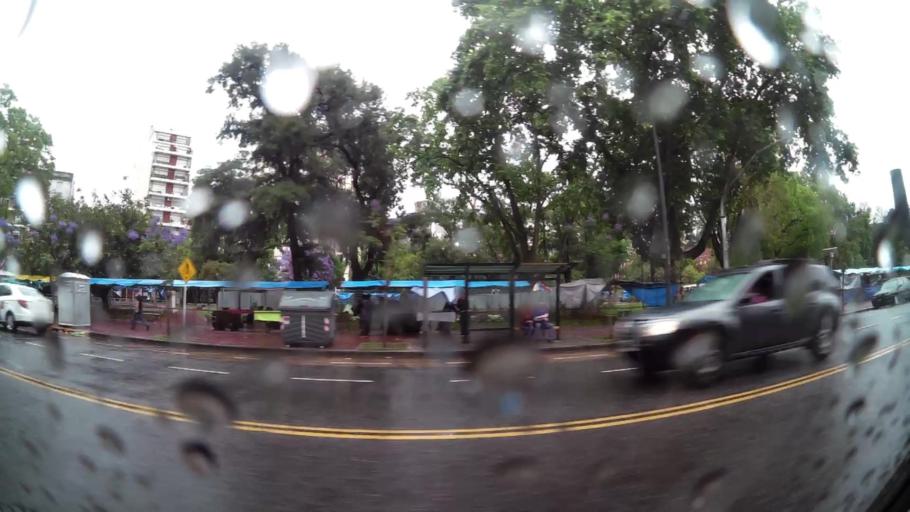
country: AR
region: Buenos Aires F.D.
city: Buenos Aires
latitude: -34.6287
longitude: -58.3698
